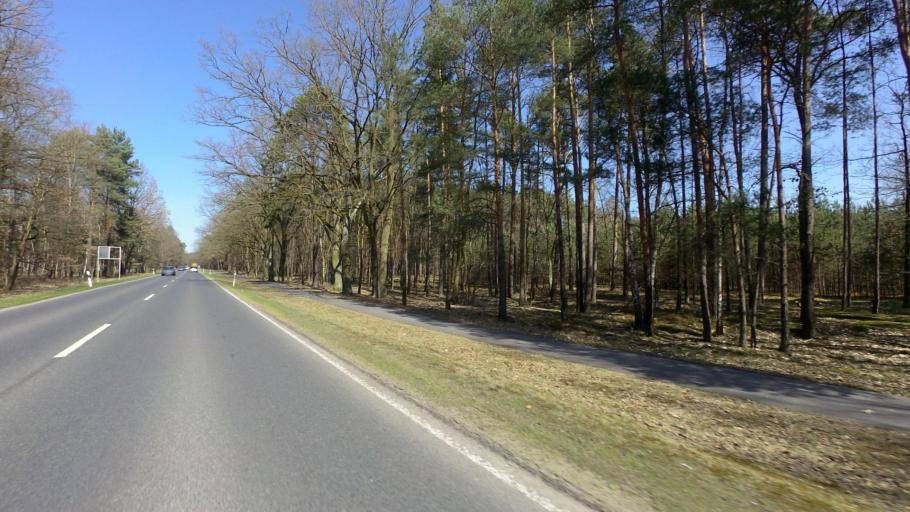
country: DE
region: Brandenburg
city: Oranienburg
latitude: 52.7842
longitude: 13.2388
